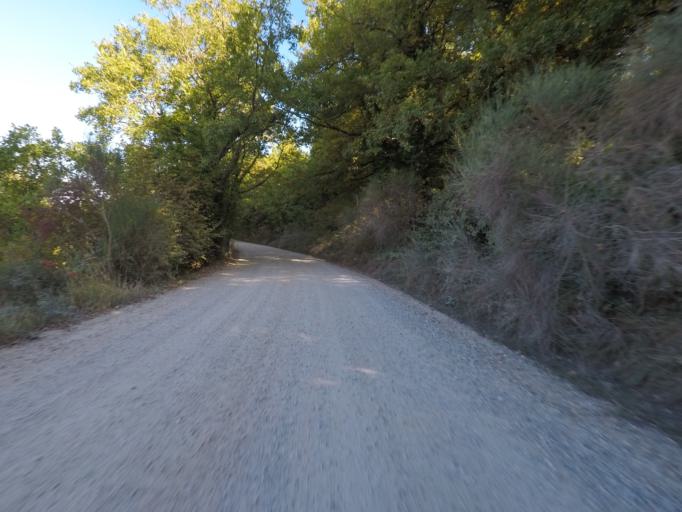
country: IT
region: Tuscany
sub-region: Provincia di Siena
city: Castellina in Chianti
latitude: 43.4305
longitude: 11.3337
